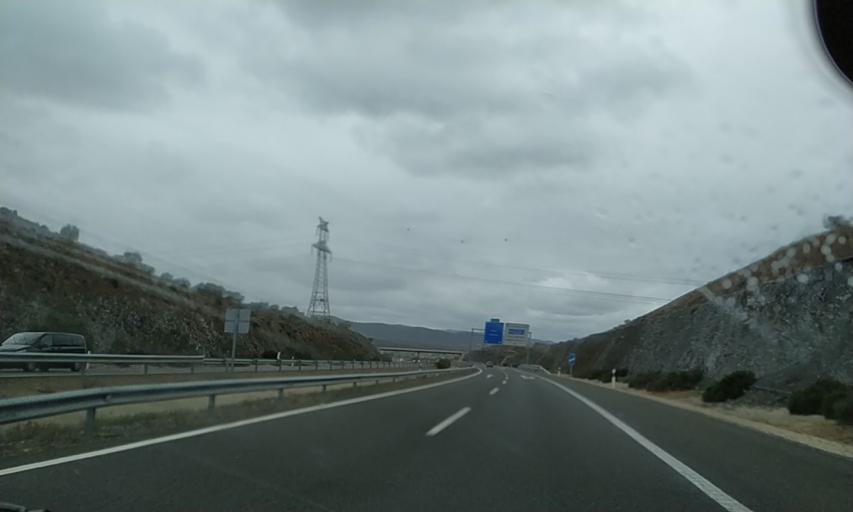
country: ES
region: Extremadura
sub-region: Provincia de Caceres
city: Plasencia
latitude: 39.9905
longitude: -6.1511
